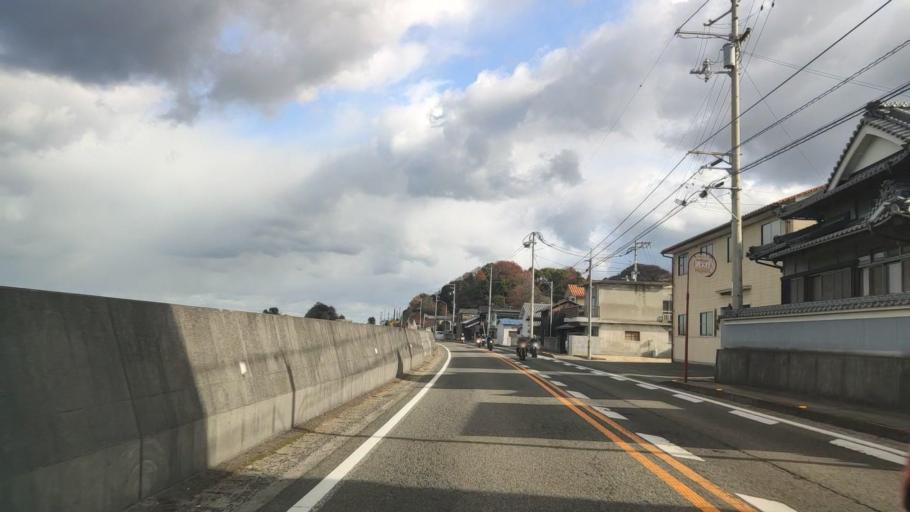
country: JP
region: Ehime
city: Hojo
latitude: 34.0001
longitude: 132.7735
